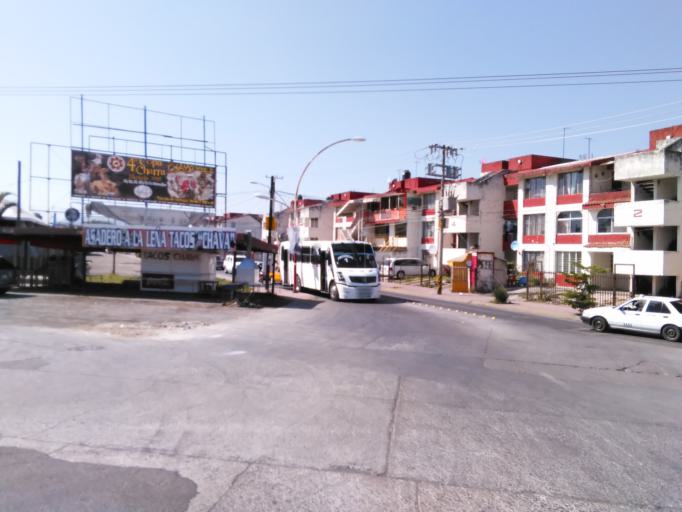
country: MX
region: Nayarit
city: Tepic
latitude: 21.4797
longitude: -104.8752
